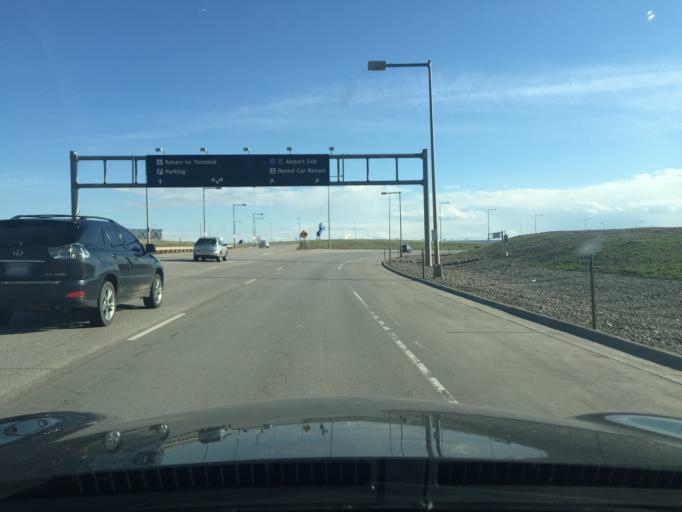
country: US
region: Colorado
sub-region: Weld County
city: Lochbuie
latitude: 39.8369
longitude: -104.6763
